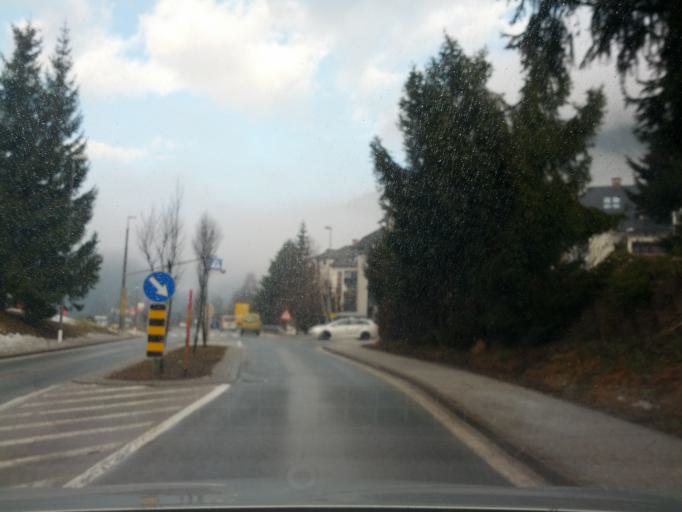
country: SI
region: Kranjska Gora
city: Kranjska Gora
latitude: 46.4873
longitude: 13.7919
